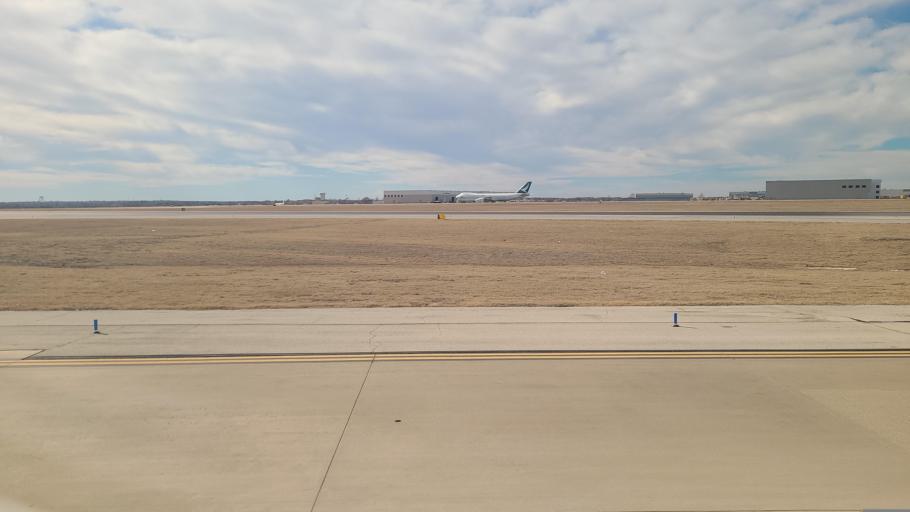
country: US
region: Texas
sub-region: Tarrant County
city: Grapevine
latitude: 32.8982
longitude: -97.0532
